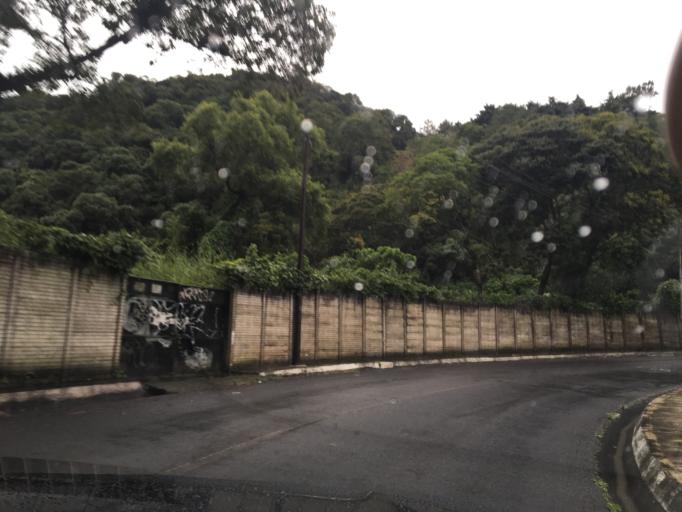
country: GT
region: Guatemala
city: Santa Catarina Pinula
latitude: 14.5536
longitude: -90.4913
